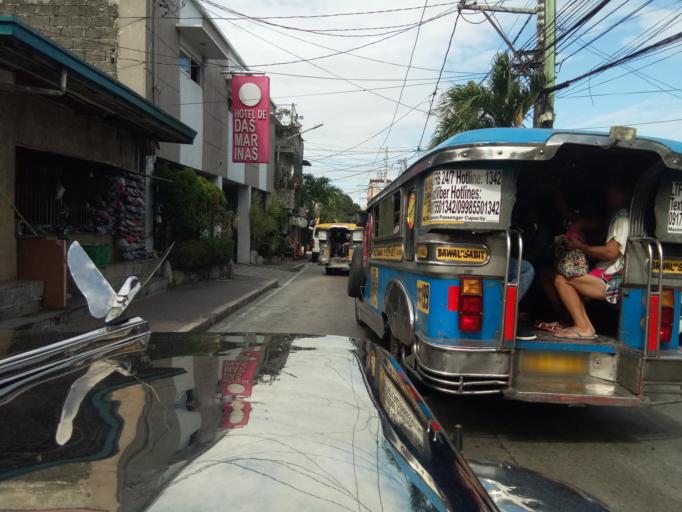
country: PH
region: Calabarzon
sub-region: Province of Cavite
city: Dasmarinas
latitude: 14.3257
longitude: 120.9374
